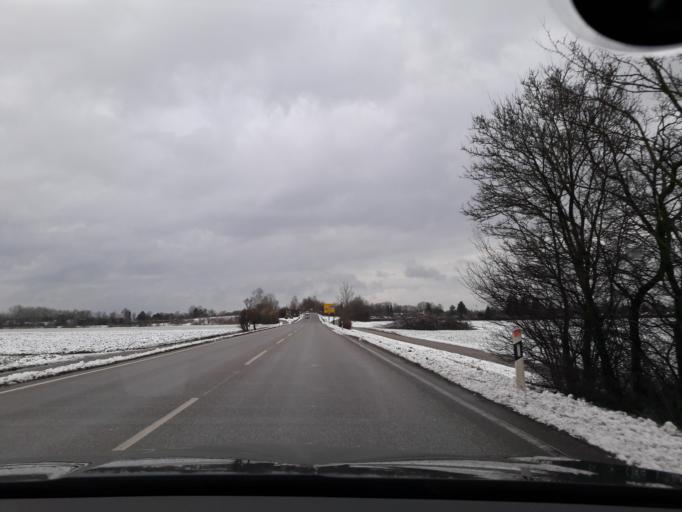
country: DE
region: Bavaria
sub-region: Upper Bavaria
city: Karlsfeld
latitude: 48.2523
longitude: 11.4727
